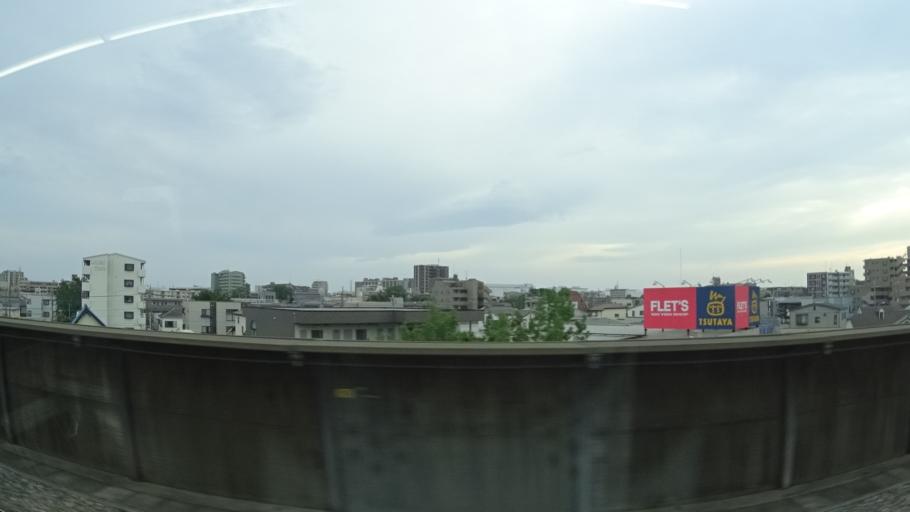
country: JP
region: Saitama
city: Shimotoda
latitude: 35.8110
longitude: 139.6743
